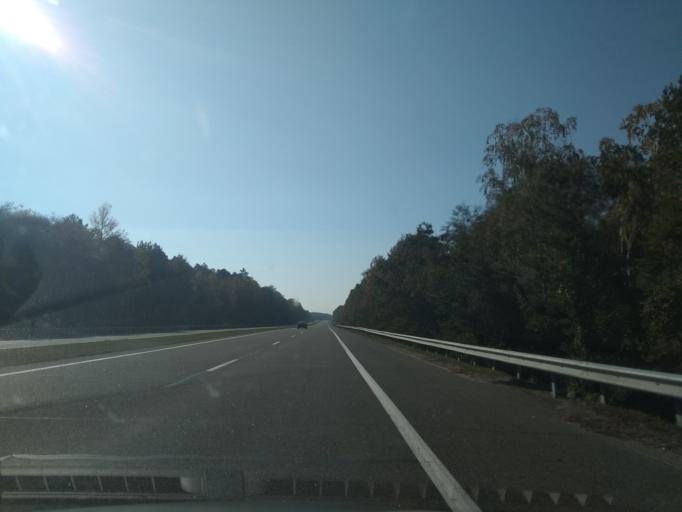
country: BY
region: Brest
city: Horad Kobryn
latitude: 52.2795
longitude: 24.5509
